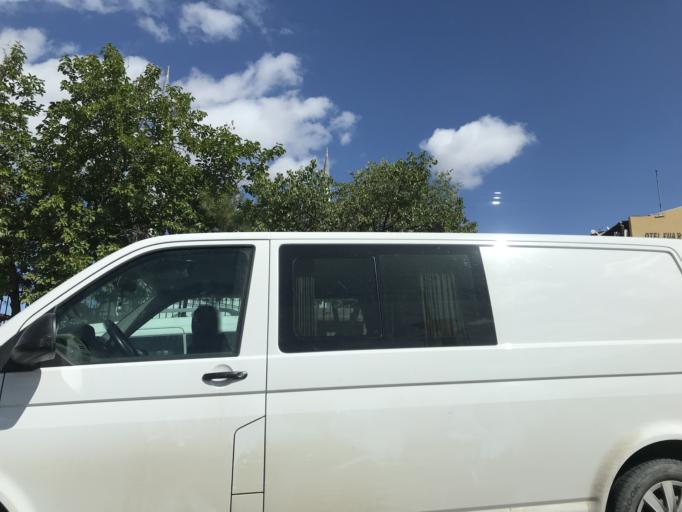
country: TR
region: Ankara
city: Ankara
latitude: 39.9350
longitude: 32.8552
